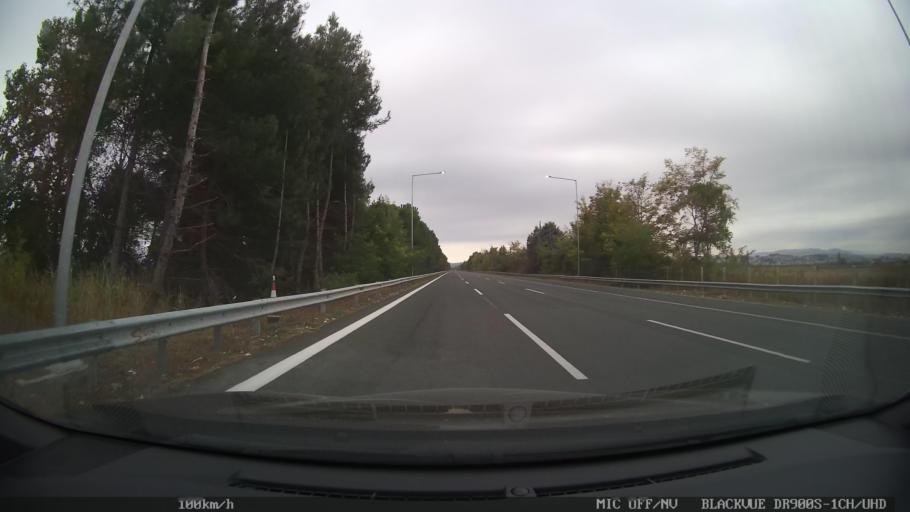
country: GR
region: Central Macedonia
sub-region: Nomos Pierias
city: Aiginio
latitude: 40.5108
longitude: 22.5693
